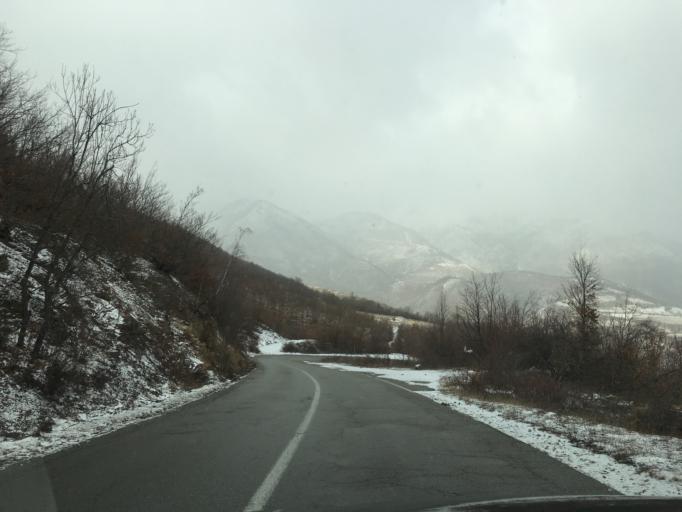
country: XK
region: Pec
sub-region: Komuna e Pejes
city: Dubova (Driloni)
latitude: 42.7517
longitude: 20.3035
